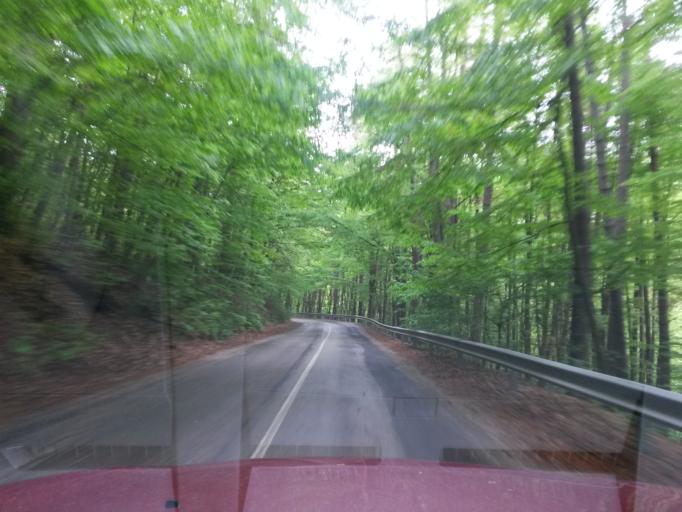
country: SK
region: Kosicky
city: Roznava
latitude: 48.5643
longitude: 20.4703
